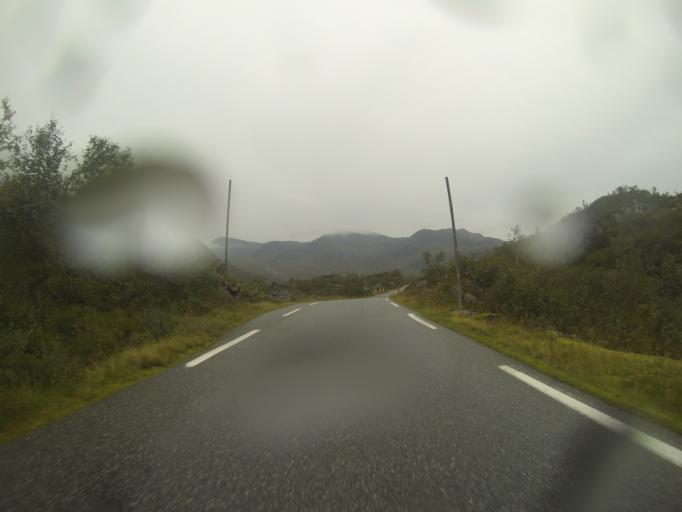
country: NO
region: Rogaland
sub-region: Sauda
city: Sauda
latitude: 59.7250
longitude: 6.5759
